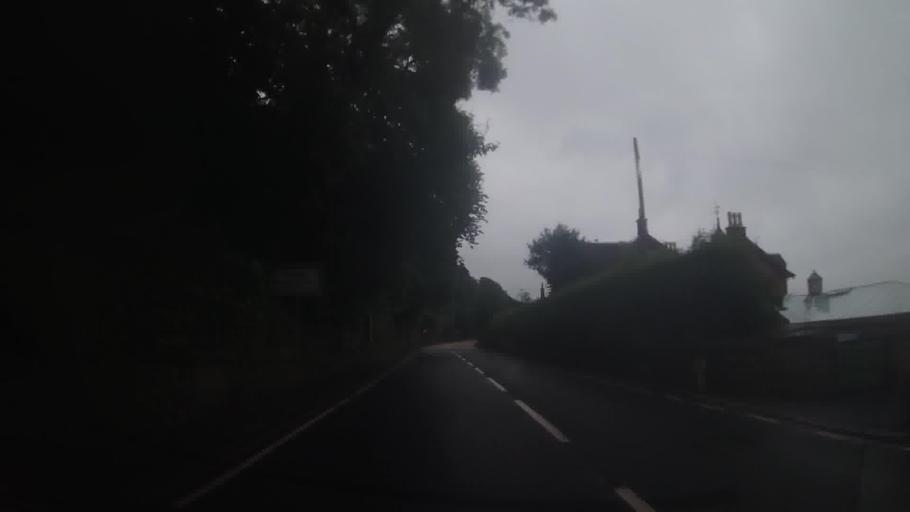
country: GB
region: Scotland
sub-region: Inverclyde
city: Wemyss Bay
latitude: 55.8704
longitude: -4.8914
